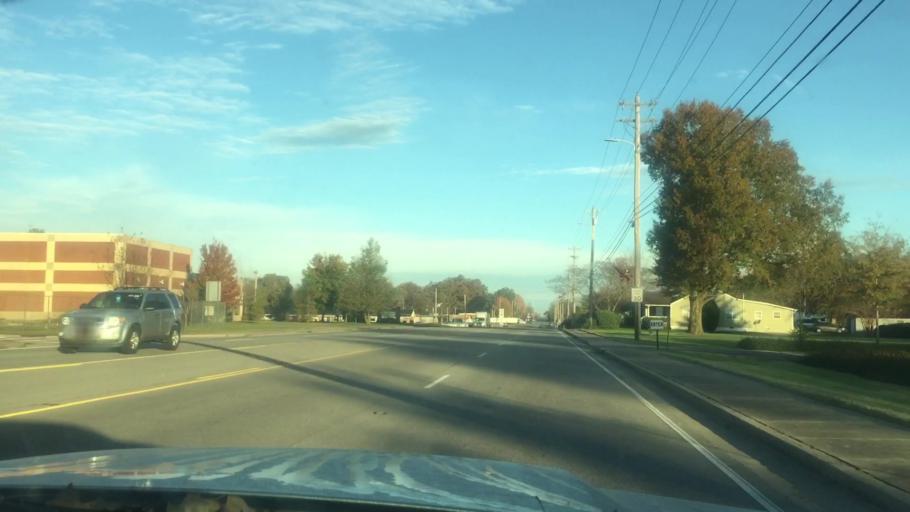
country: US
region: Tennessee
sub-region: Coffee County
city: Tullahoma
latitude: 35.3520
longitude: -86.2026
